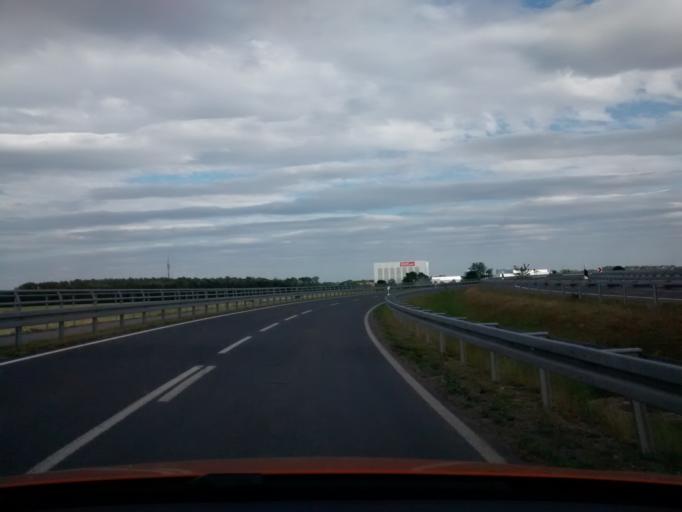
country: DE
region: Brandenburg
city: Schonefeld
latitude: 52.3775
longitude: 13.5469
